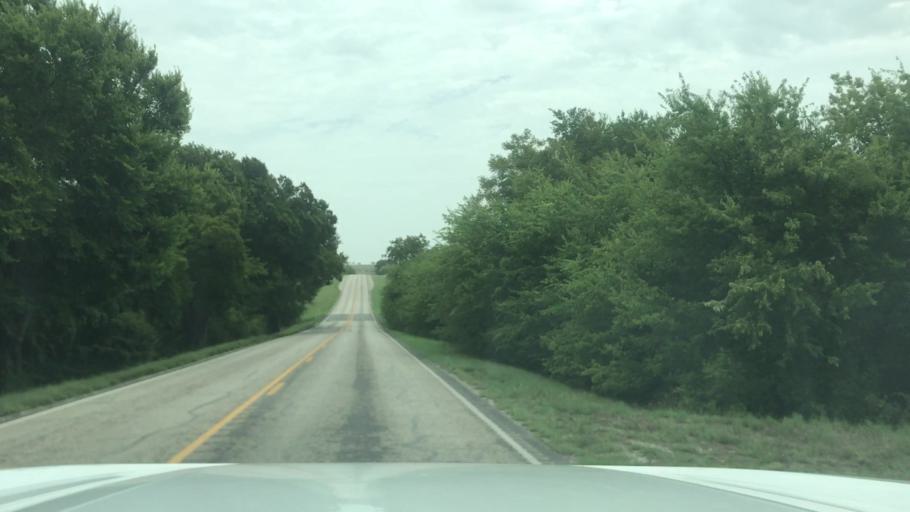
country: US
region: Texas
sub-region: Erath County
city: Dublin
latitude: 32.0578
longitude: -98.1975
